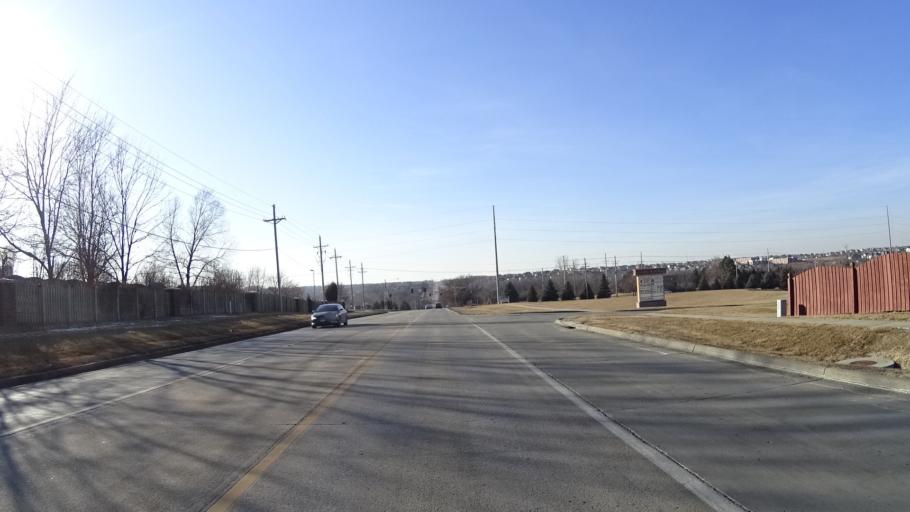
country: US
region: Nebraska
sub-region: Douglas County
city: Bennington
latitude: 41.3066
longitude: -96.1364
